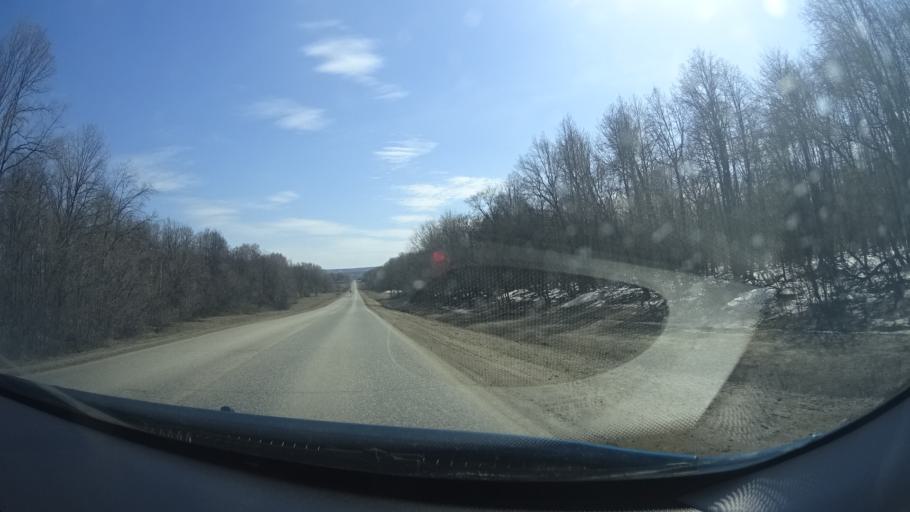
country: RU
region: Bashkortostan
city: Oktyabr'skiy
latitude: 54.4579
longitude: 53.5822
